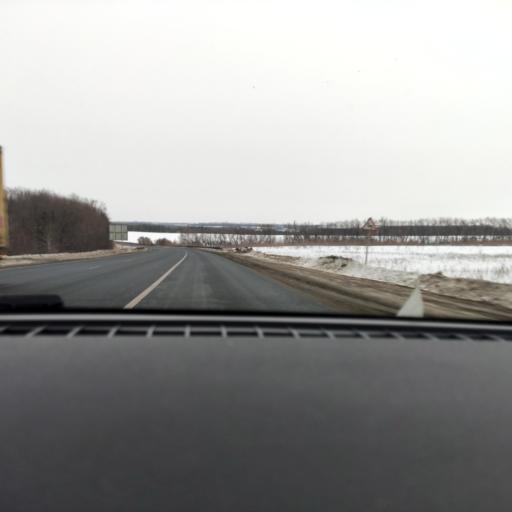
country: RU
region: Samara
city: Novosemeykino
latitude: 53.3477
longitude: 50.4508
